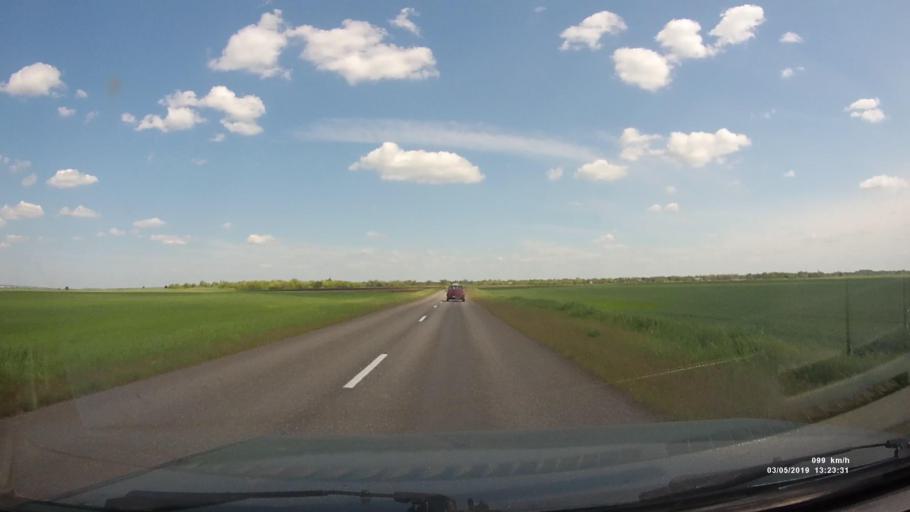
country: RU
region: Rostov
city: Semikarakorsk
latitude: 47.5625
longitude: 40.7839
